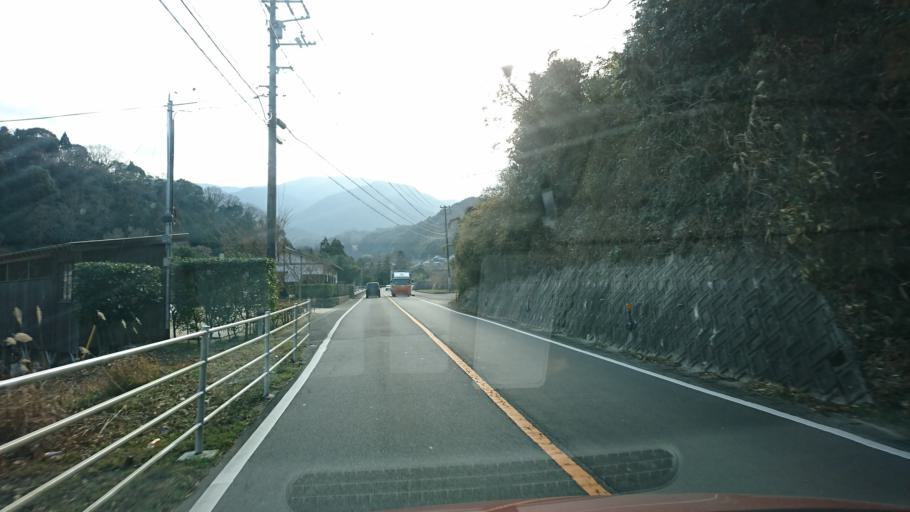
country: JP
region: Ehime
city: Hojo
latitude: 33.9826
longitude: 132.9072
